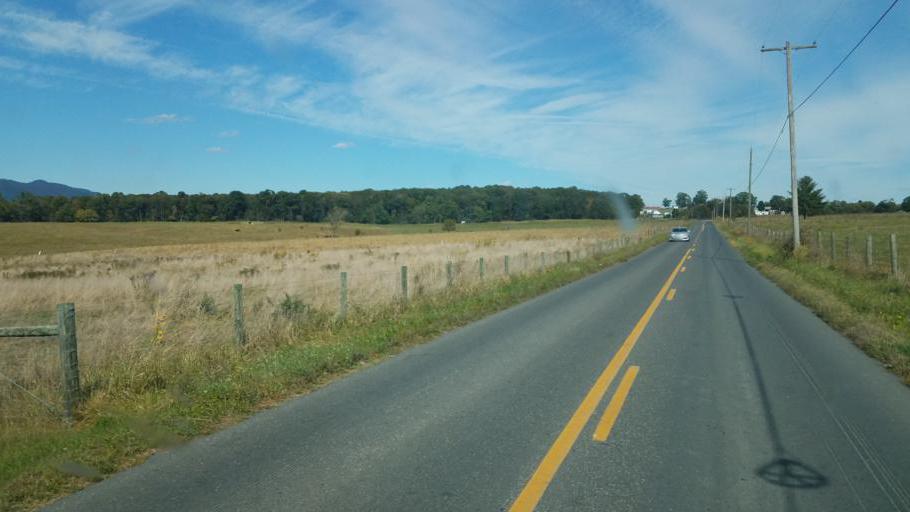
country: US
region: Virginia
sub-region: Page County
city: Stanley
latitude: 38.5996
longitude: -78.5520
